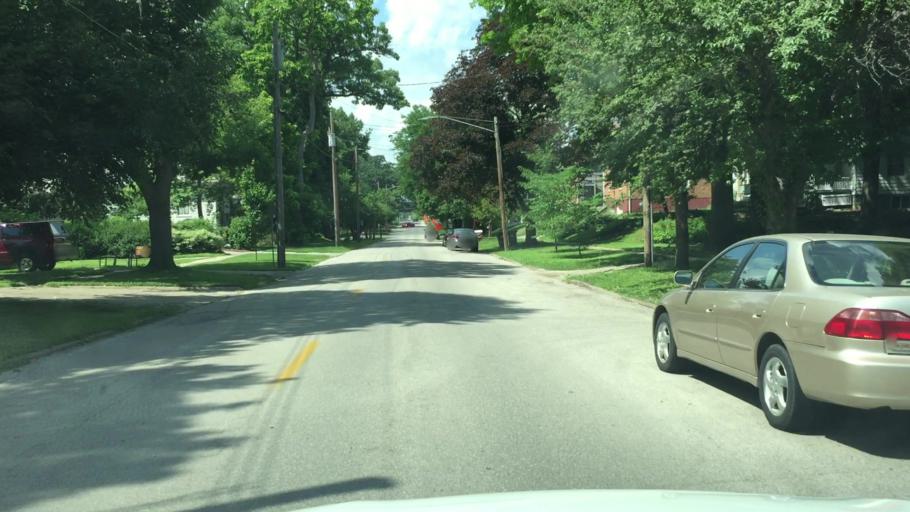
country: US
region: Iowa
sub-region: Johnson County
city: Iowa City
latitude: 41.6556
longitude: -91.5229
